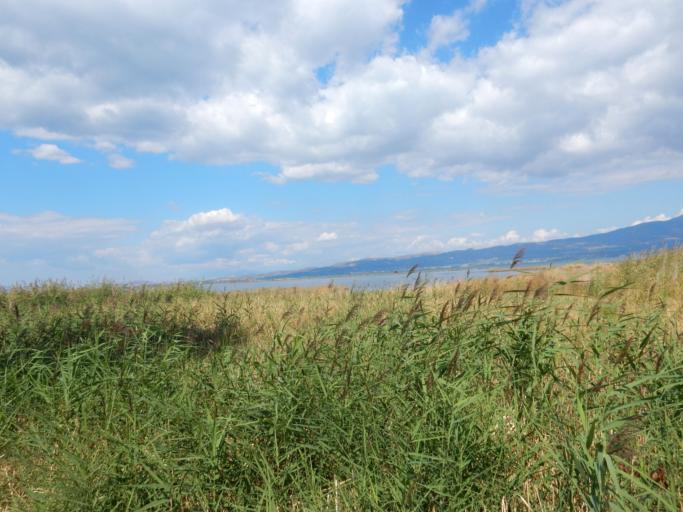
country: GR
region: Attica
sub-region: Nomarchia Anatolikis Attikis
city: Skala Oropou
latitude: 38.3345
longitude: 23.7724
